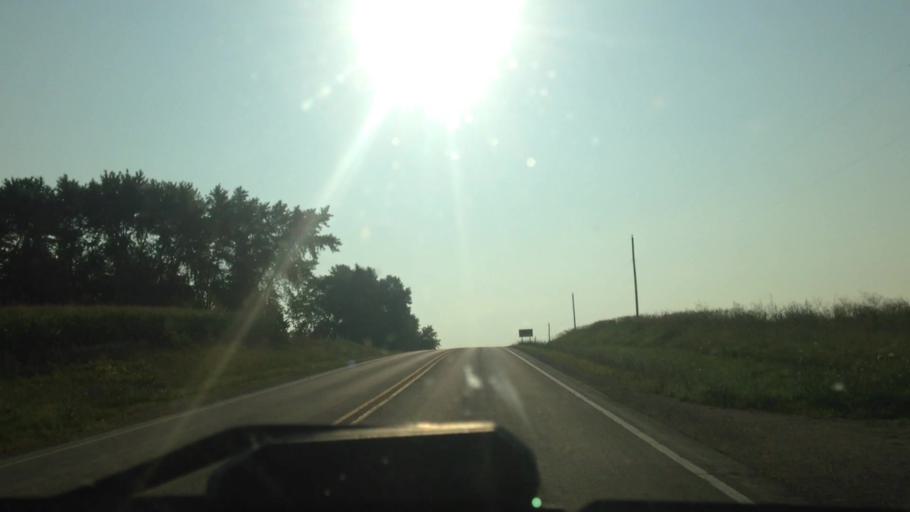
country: US
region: Wisconsin
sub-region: Dodge County
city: Theresa
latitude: 43.5363
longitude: -88.4534
